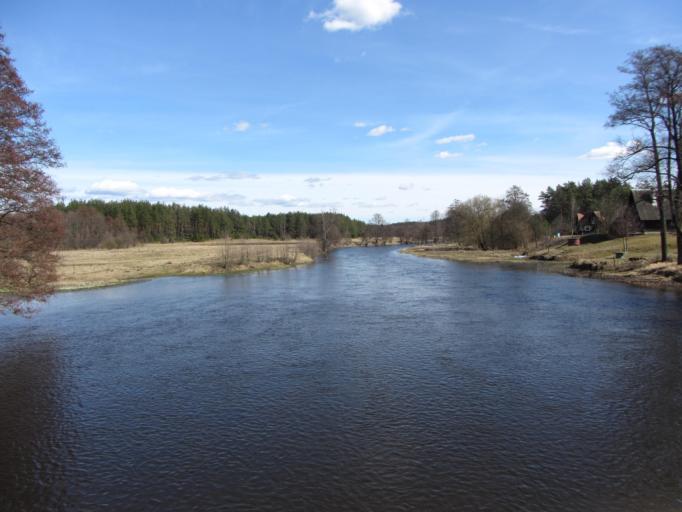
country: LT
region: Alytaus apskritis
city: Varena
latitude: 54.3114
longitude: 24.7156
